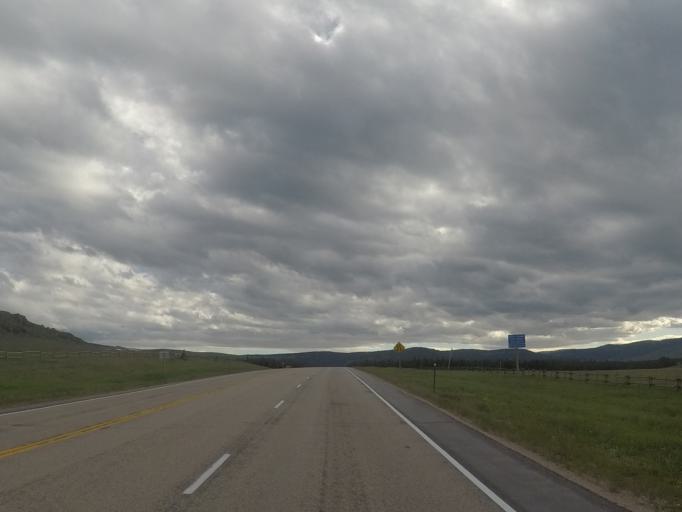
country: US
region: Wyoming
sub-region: Sheridan County
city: Sheridan
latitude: 44.7833
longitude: -107.5005
